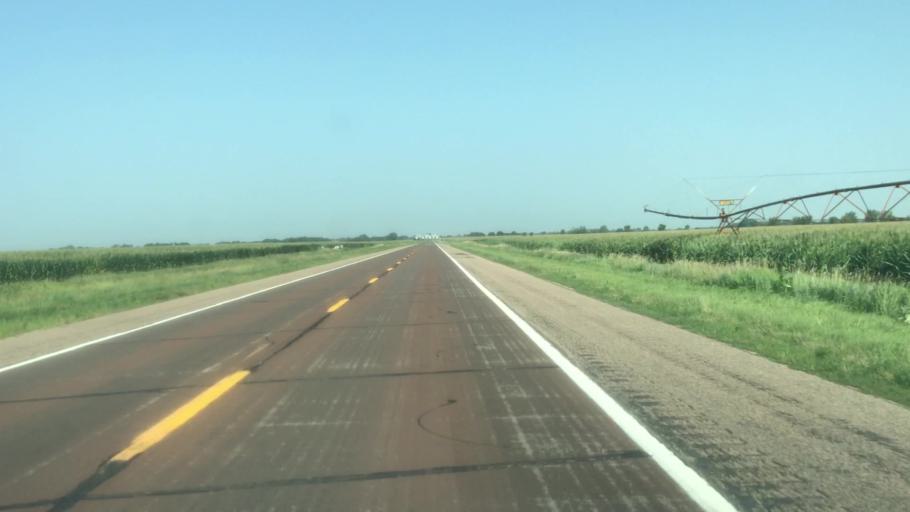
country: US
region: Nebraska
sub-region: Hall County
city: Wood River
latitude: 40.9778
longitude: -98.5169
